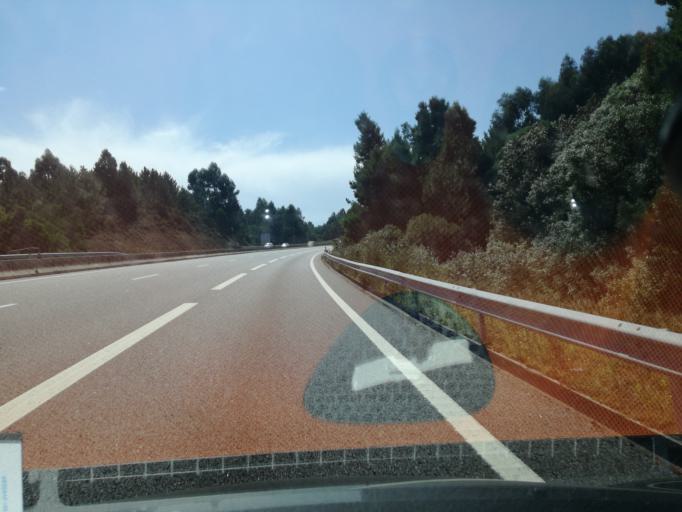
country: PT
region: Viana do Castelo
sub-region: Caminha
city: Vila Praia de Ancora
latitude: 41.7875
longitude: -8.7894
